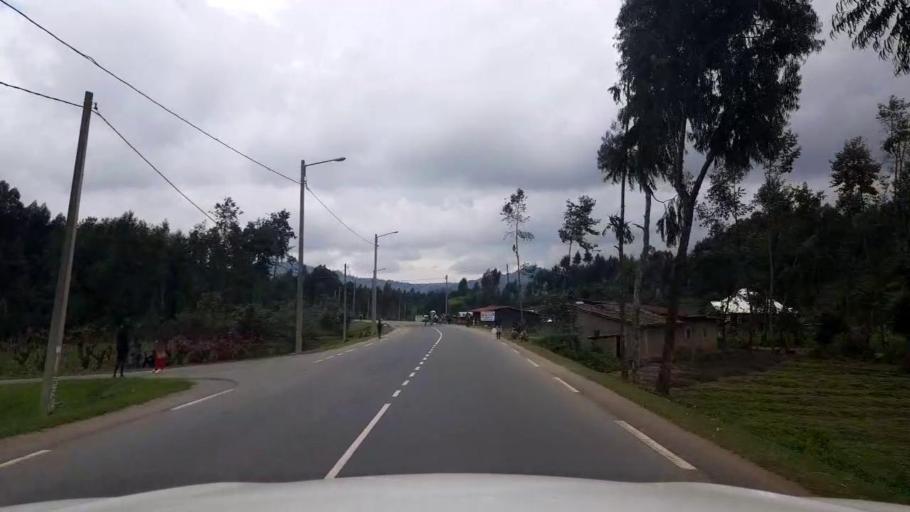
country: RW
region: Northern Province
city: Musanze
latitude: -1.6186
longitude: 29.5040
